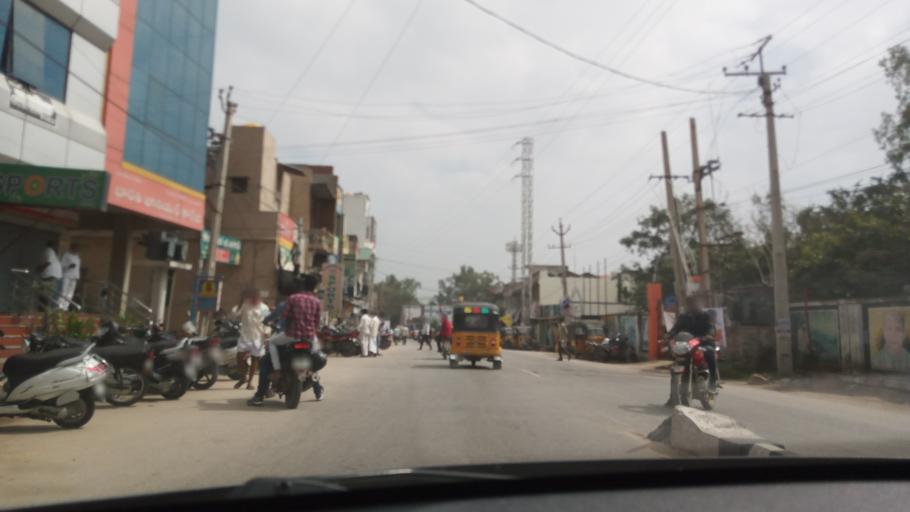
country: IN
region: Andhra Pradesh
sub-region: Chittoor
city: Madanapalle
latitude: 13.5558
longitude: 78.4995
